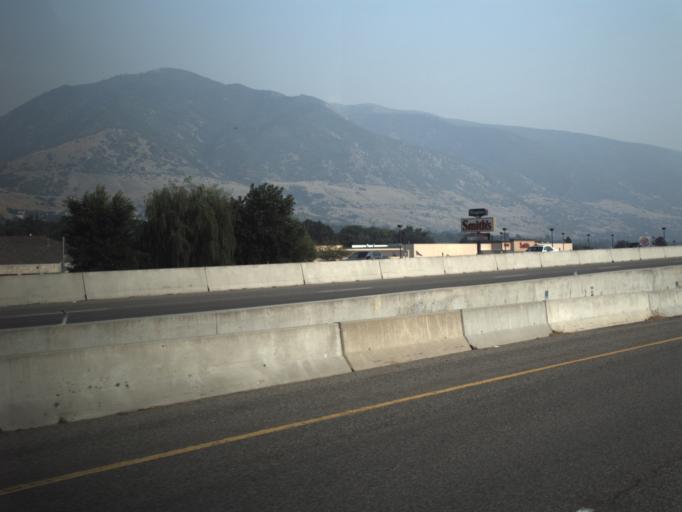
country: US
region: Utah
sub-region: Davis County
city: Fruit Heights
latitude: 41.0040
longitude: -111.9097
